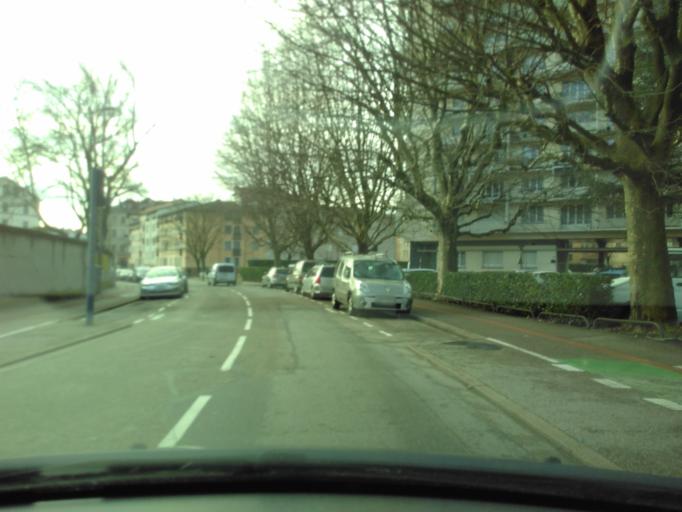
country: FR
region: Rhone-Alpes
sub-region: Departement de l'Isere
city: La Tronche
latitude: 45.1935
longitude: 5.7354
